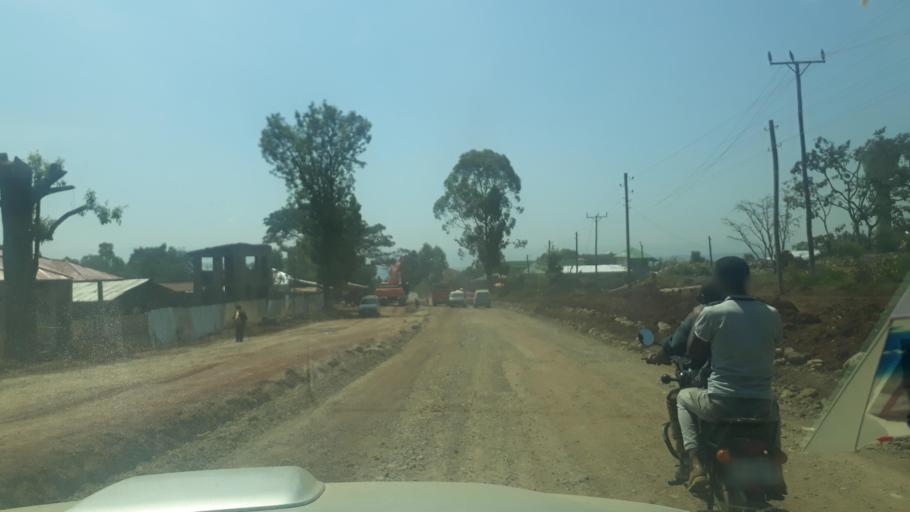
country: ET
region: Oromiya
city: Jima
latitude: 7.7076
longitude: 36.8056
